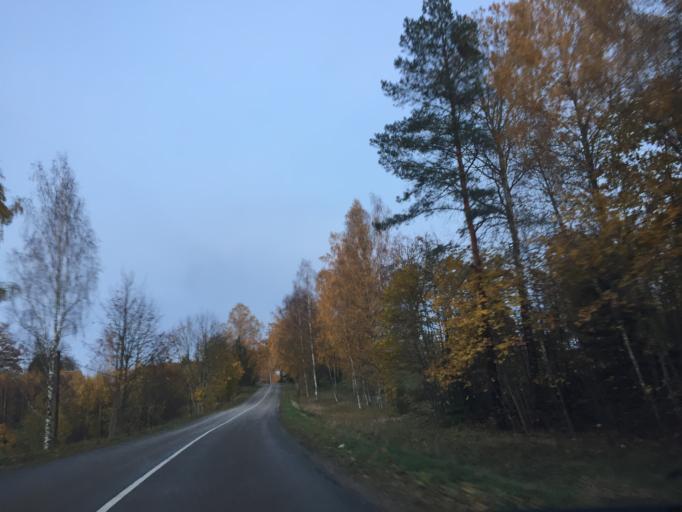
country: LV
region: Cesu Rajons
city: Cesis
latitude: 57.3116
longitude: 25.1813
